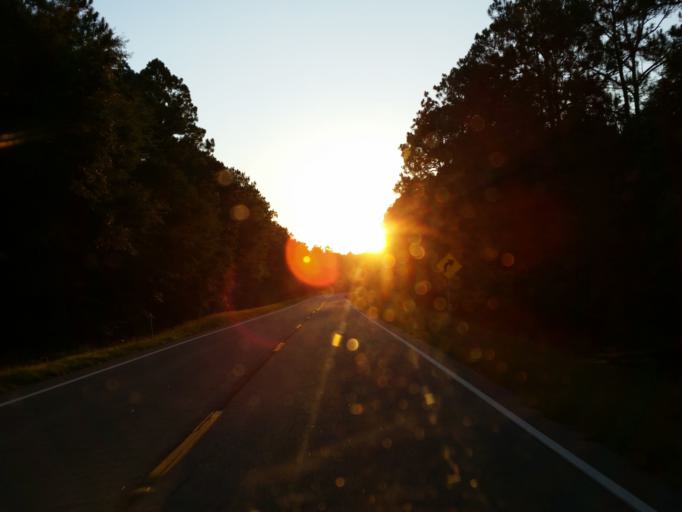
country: US
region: Georgia
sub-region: Berrien County
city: Nashville
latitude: 31.2185
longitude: -83.2839
